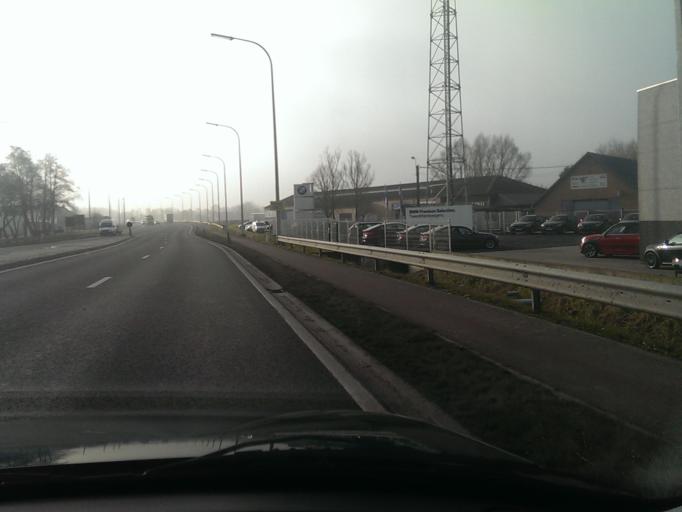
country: BE
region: Flanders
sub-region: Provincie West-Vlaanderen
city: Roeselare
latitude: 50.9331
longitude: 3.1018
